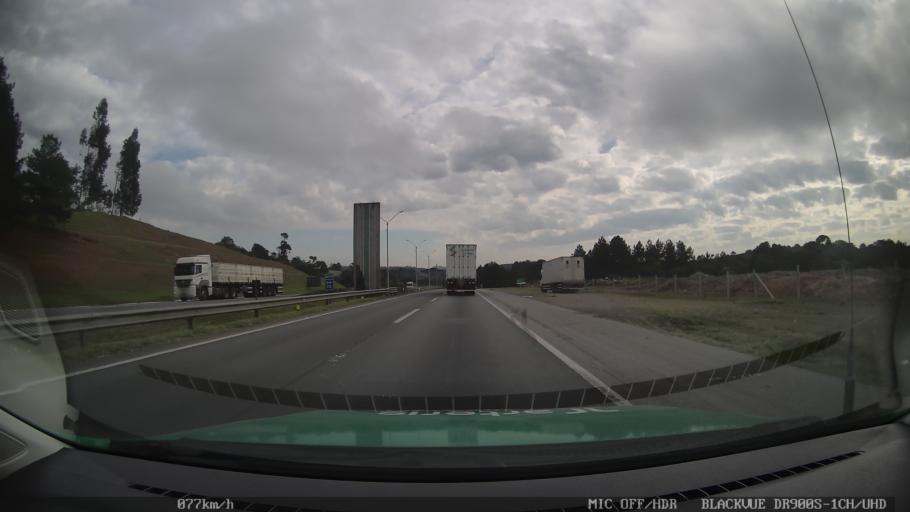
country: BR
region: Parana
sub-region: Quatro Barras
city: Quatro Barras
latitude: -25.3513
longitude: -49.0422
